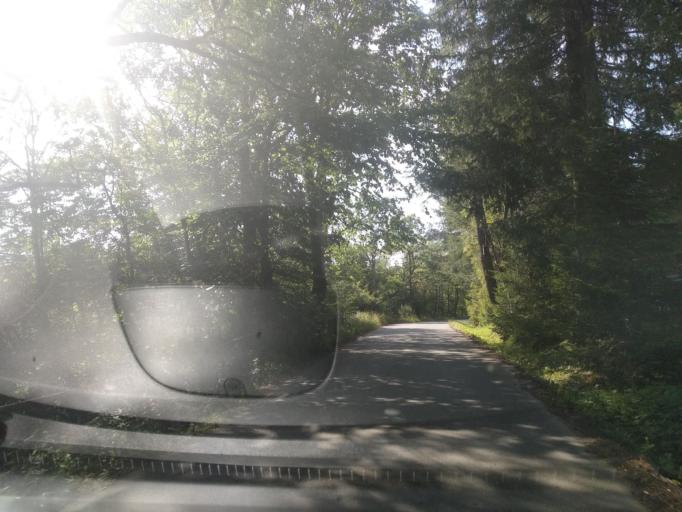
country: PL
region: Subcarpathian Voivodeship
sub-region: Powiat krosnienski
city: Jasliska
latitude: 49.4247
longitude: 21.8543
